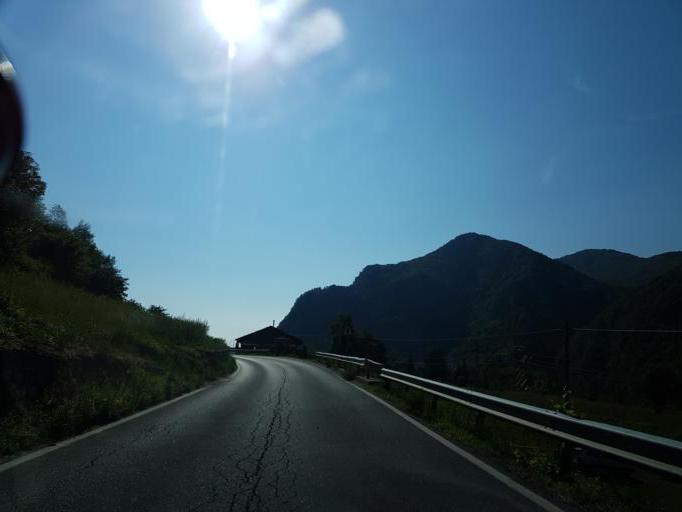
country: IT
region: Piedmont
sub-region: Provincia di Cuneo
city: San Damiano Macra
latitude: 44.4884
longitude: 7.2468
